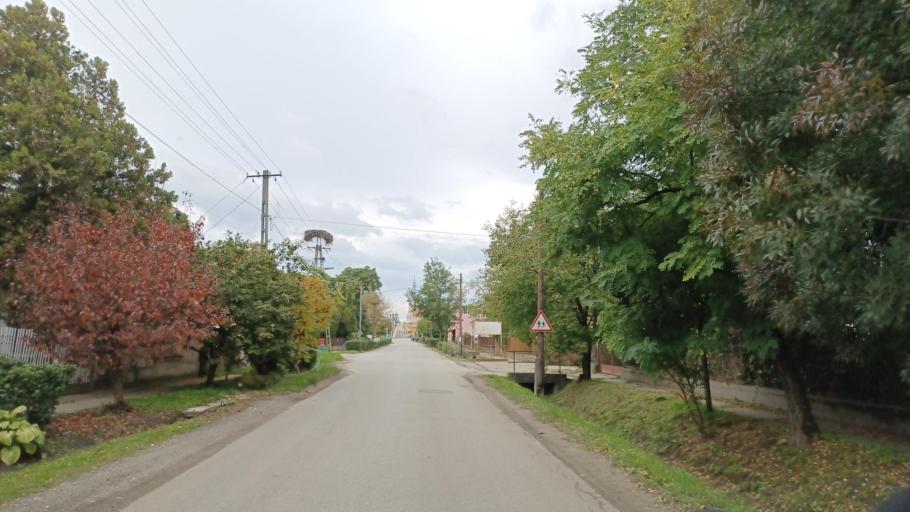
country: HU
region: Tolna
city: Simontornya
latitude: 46.7492
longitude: 18.5563
